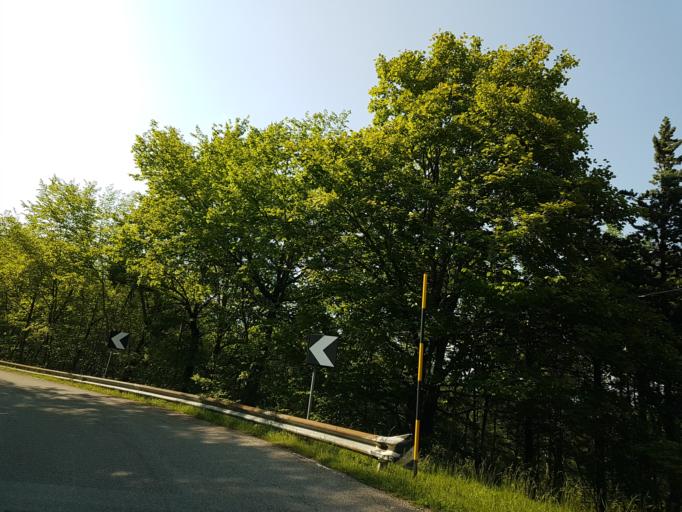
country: IT
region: Emilia-Romagna
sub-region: Forli-Cesena
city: San Piero in Bagno
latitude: 43.8137
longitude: 11.9178
